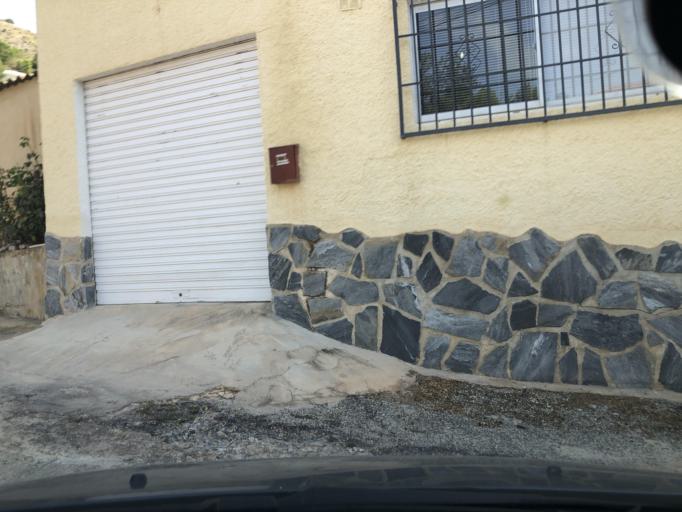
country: ES
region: Valencia
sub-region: Provincia de Alicante
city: Callosa d'En Sarria
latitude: 38.6527
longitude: -0.1280
